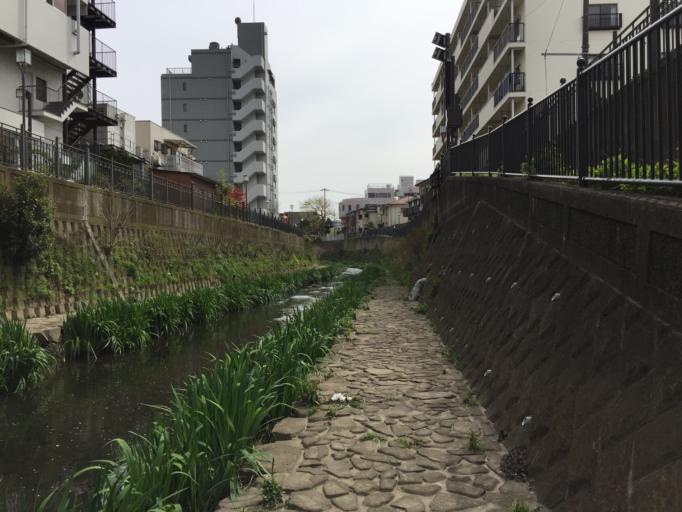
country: JP
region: Kanagawa
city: Yokohama
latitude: 35.4100
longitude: 139.5951
